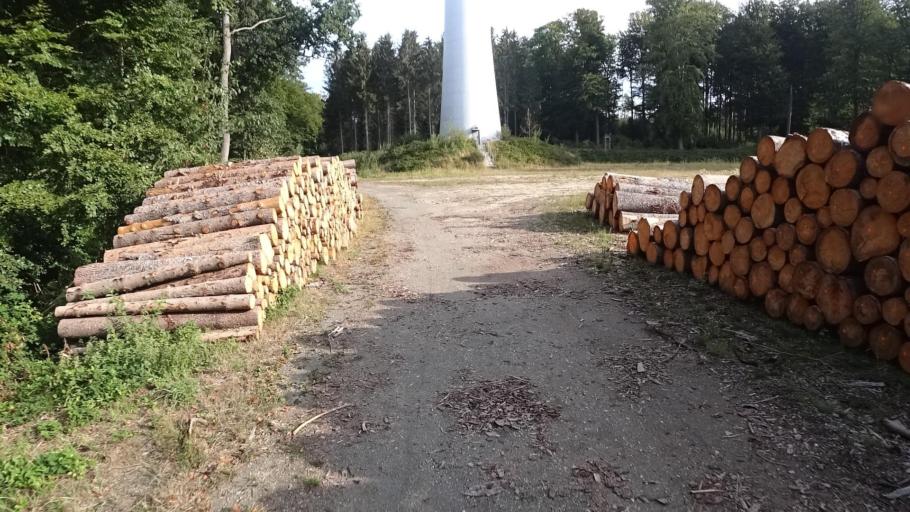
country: DE
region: Rheinland-Pfalz
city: Niederkumbd
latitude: 50.0185
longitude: 7.5103
